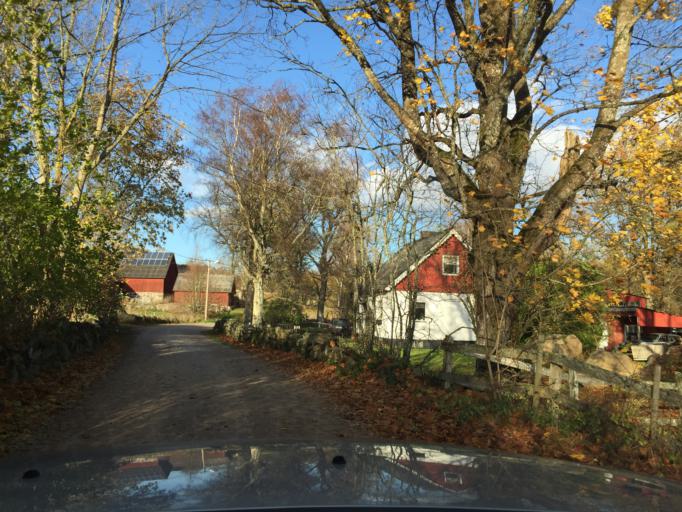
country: SE
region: Skane
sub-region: Hassleholms Kommun
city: Tormestorp
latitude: 56.0673
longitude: 13.7275
